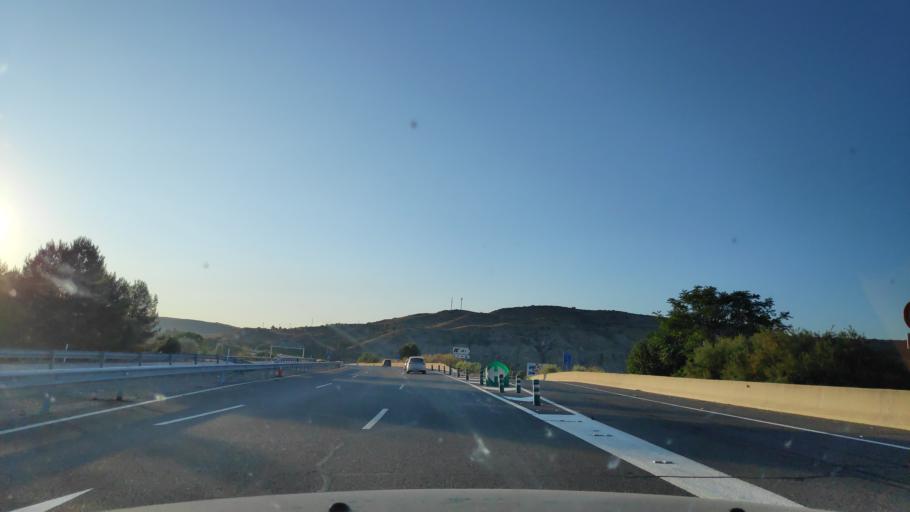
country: ES
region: Madrid
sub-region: Provincia de Madrid
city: Perales de Tajuna
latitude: 40.2230
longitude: -3.3314
